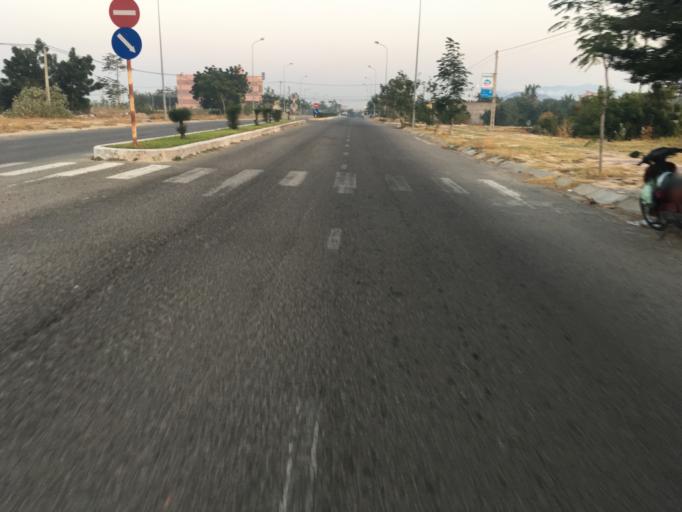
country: VN
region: Ninh Thuan
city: Phan Rang-Thap Cham
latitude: 11.5563
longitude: 109.0228
